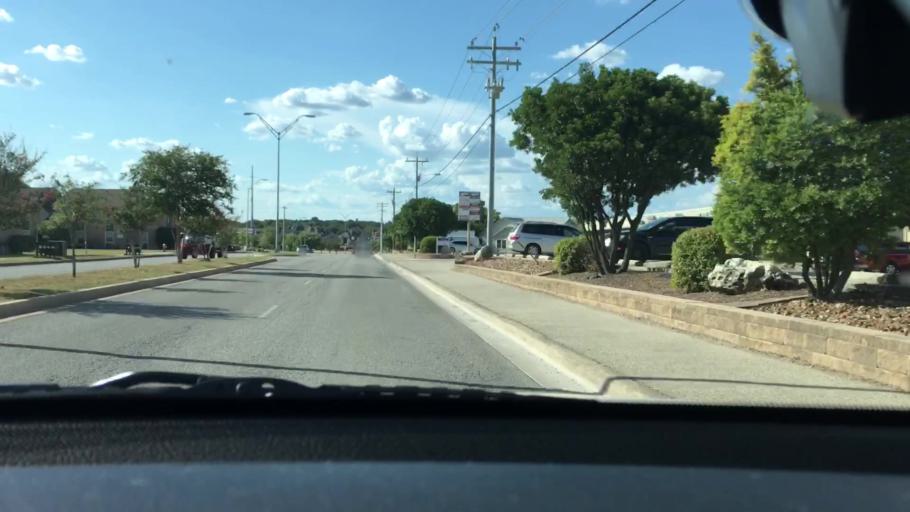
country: US
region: Texas
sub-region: Guadalupe County
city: Schertz
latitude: 29.5661
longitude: -98.2708
